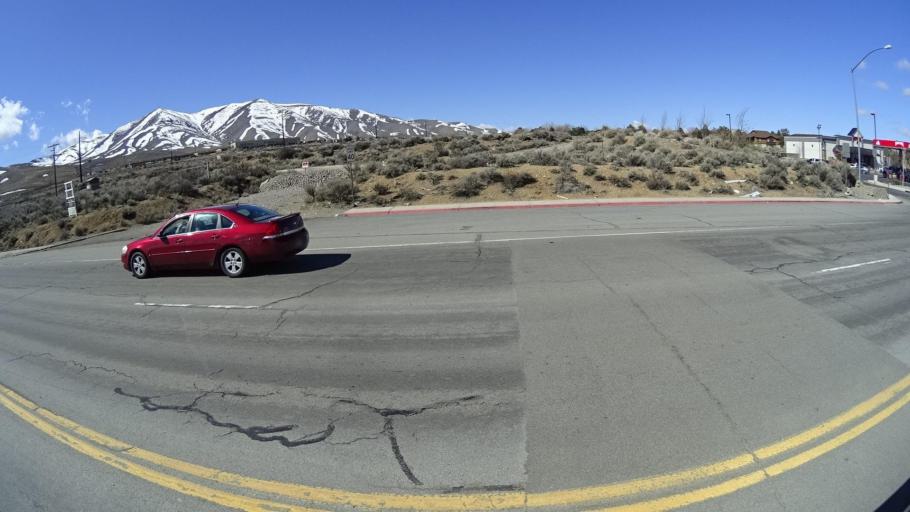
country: US
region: Nevada
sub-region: Washoe County
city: Lemmon Valley
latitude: 39.6214
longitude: -119.8828
